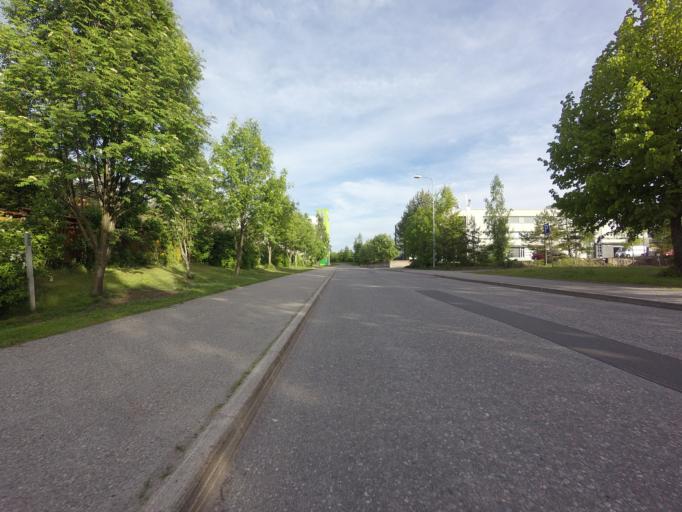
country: FI
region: Uusimaa
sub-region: Helsinki
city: Koukkuniemi
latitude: 60.1633
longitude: 24.7262
